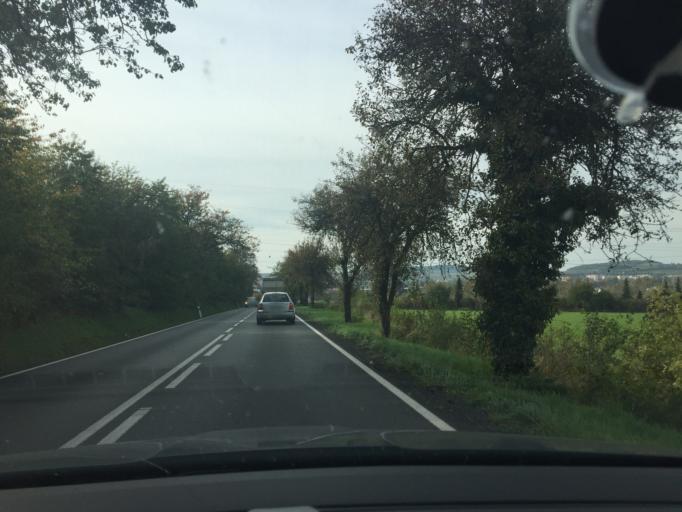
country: CZ
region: Central Bohemia
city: Cirkvice
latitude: 49.9452
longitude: 15.3022
